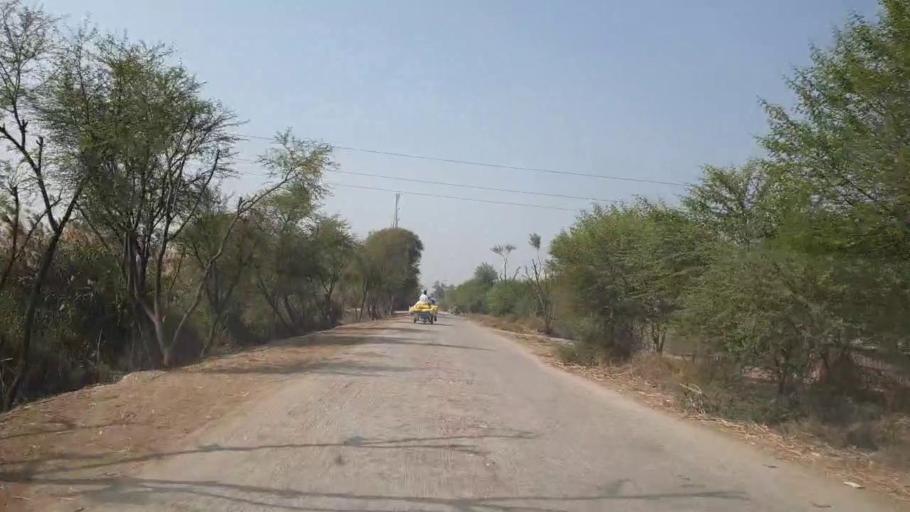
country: PK
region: Sindh
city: Mirpur Khas
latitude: 25.7066
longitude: 69.1324
